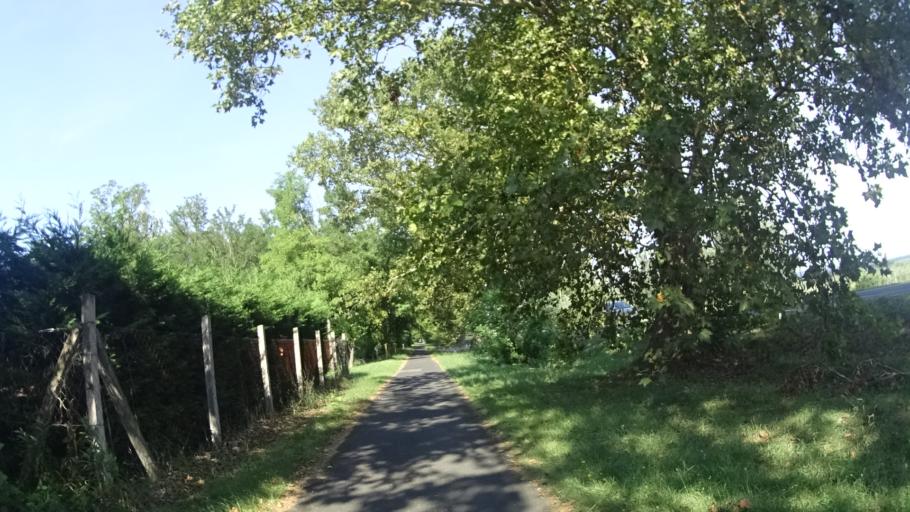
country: HU
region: Somogy
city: Balatonszarszo
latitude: 46.8207
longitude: 17.8031
